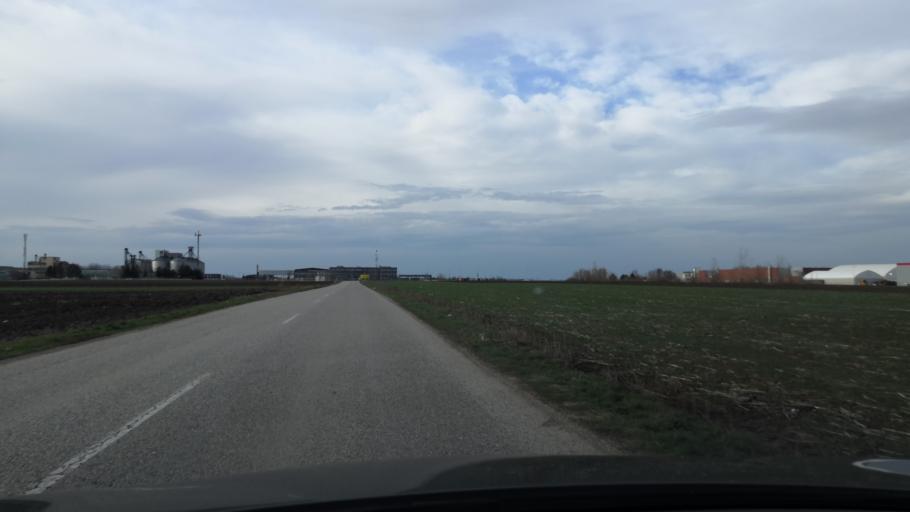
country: RS
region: Autonomna Pokrajina Vojvodina
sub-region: Sremski Okrug
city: Ingija
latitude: 45.0512
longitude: 20.1064
